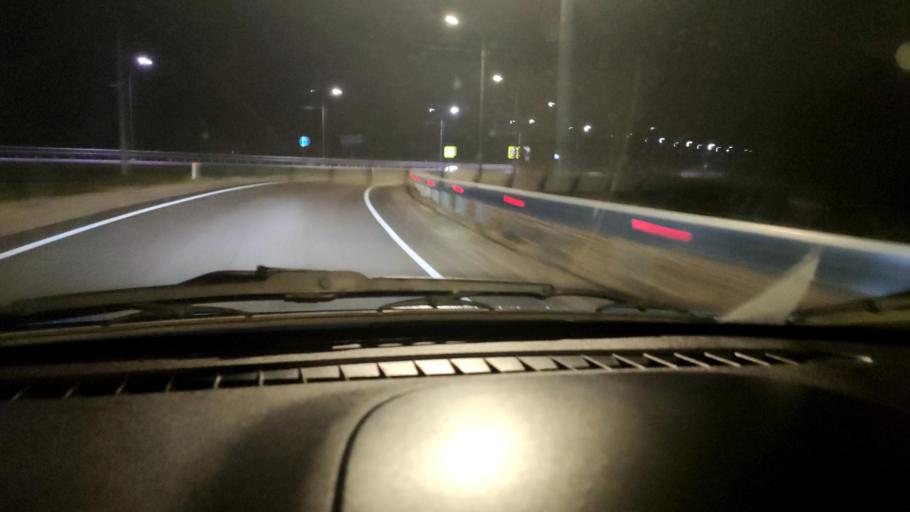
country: RU
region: Voronezj
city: Ramon'
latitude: 51.8884
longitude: 39.2166
